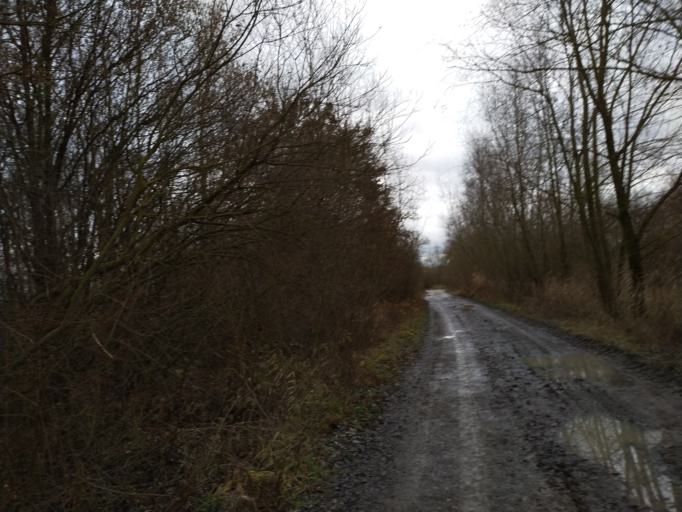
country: DE
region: Bavaria
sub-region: Swabia
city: Bachingen an der Brenz
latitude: 48.5021
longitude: 10.2998
